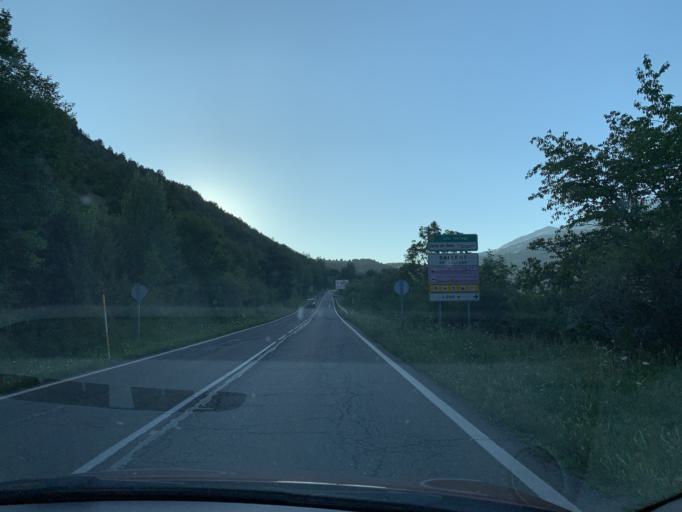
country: ES
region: Aragon
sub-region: Provincia de Huesca
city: Sallent de Gallego
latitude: 42.7595
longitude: -0.3299
